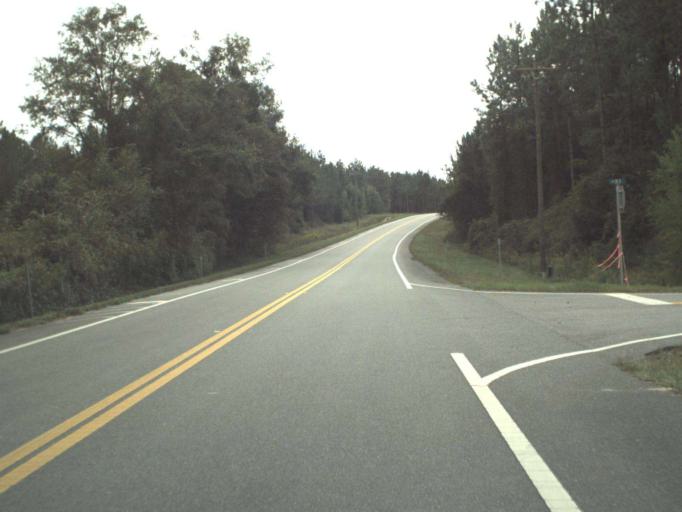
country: US
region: Florida
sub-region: Calhoun County
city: Blountstown
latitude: 30.3579
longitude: -85.2122
